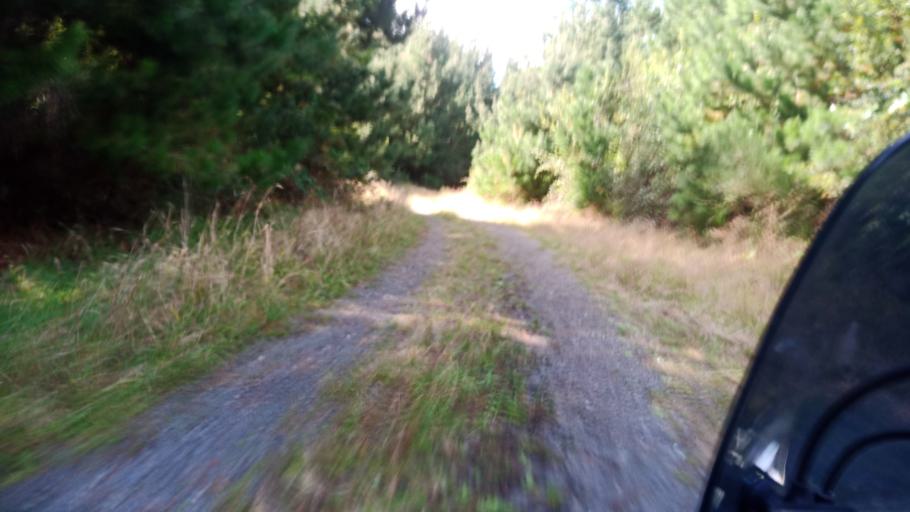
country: NZ
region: Hawke's Bay
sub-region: Wairoa District
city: Wairoa
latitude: -39.0049
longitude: 177.0825
